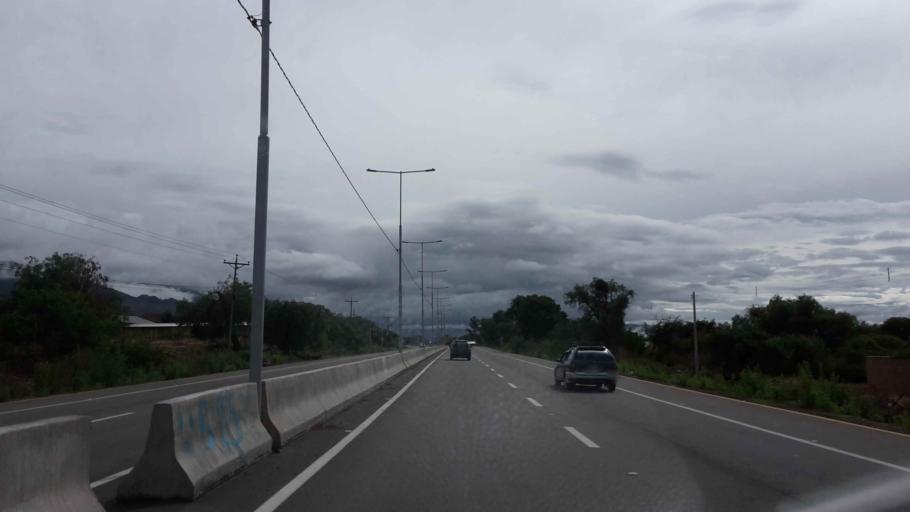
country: BO
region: Cochabamba
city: Tarata
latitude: -17.5432
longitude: -65.9992
